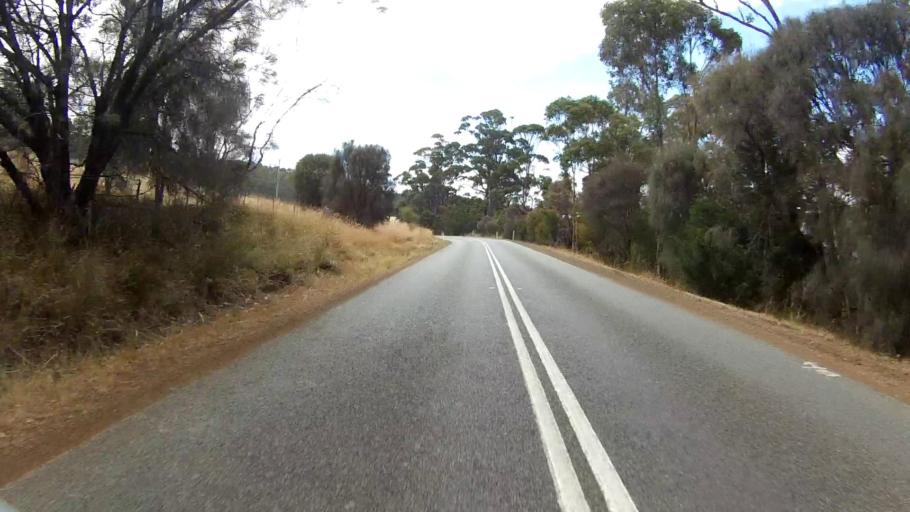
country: AU
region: Tasmania
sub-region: Sorell
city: Sorell
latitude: -42.2358
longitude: 148.0162
